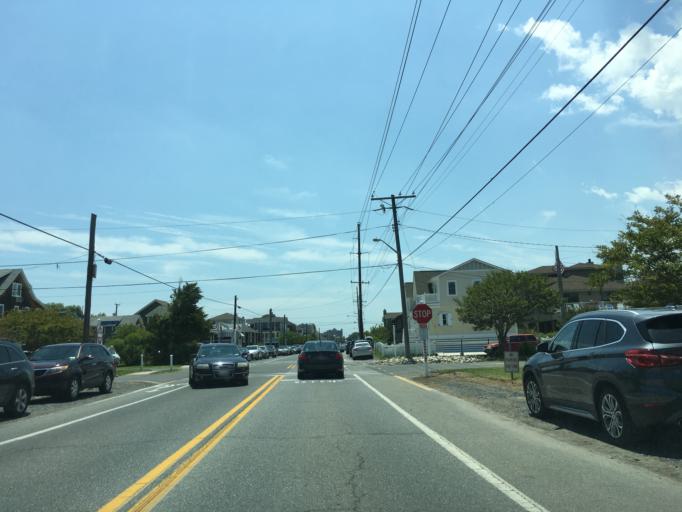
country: US
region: Delaware
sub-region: Sussex County
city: Bethany Beach
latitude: 38.5434
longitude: -75.0579
